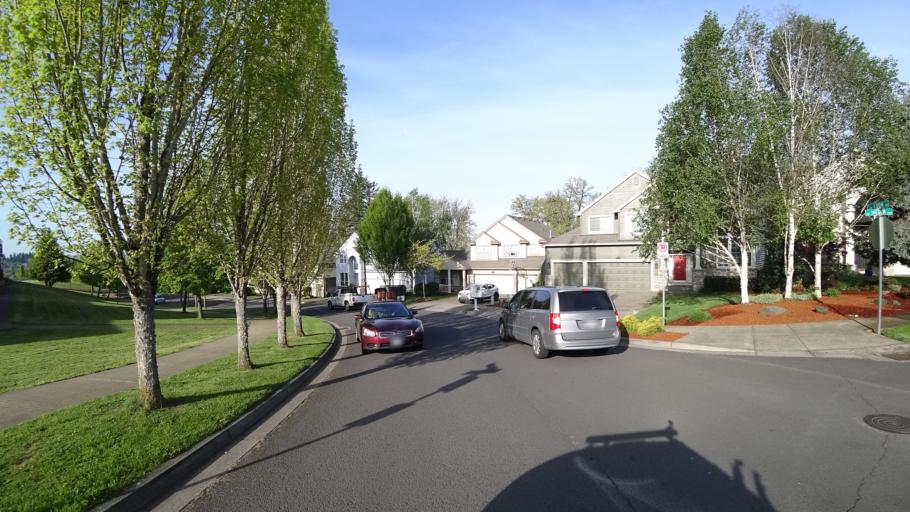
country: US
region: Oregon
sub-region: Washington County
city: King City
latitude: 45.4313
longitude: -122.8458
